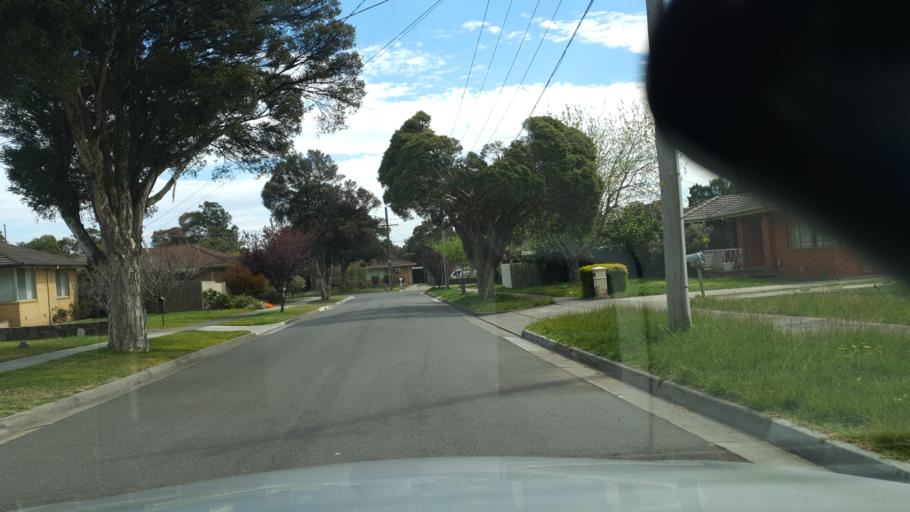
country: AU
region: Victoria
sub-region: Greater Dandenong
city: Springvale
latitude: -37.9232
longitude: 145.1640
